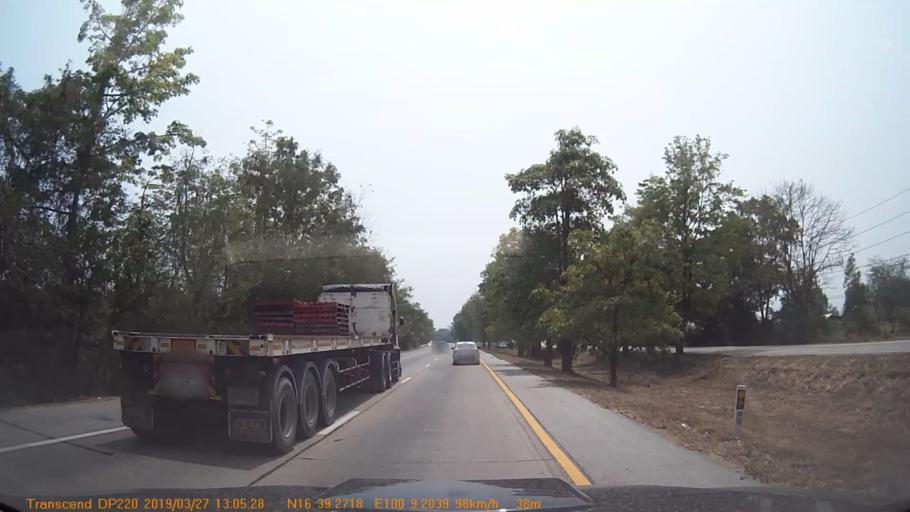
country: TH
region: Phitsanulok
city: Bang Rakam
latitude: 16.6545
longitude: 100.1534
